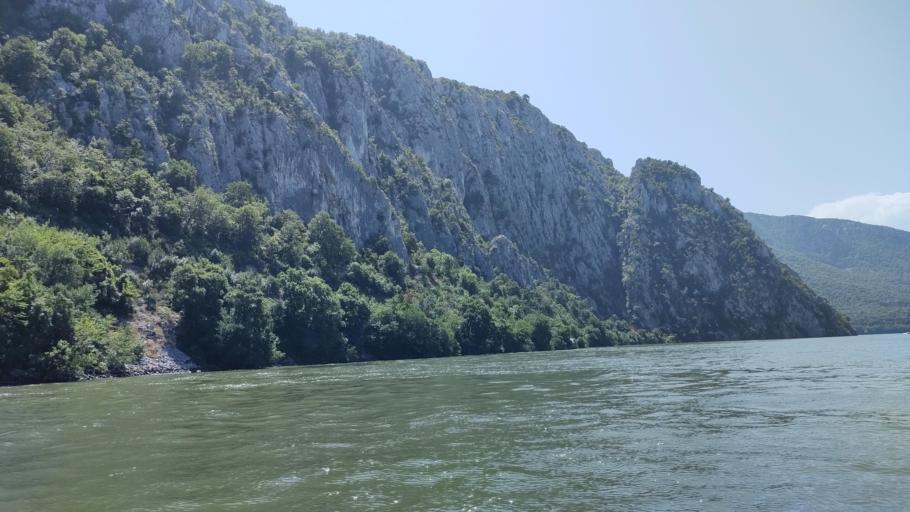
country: RO
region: Mehedinti
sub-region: Comuna Dubova
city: Dubova
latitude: 44.6191
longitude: 22.2733
